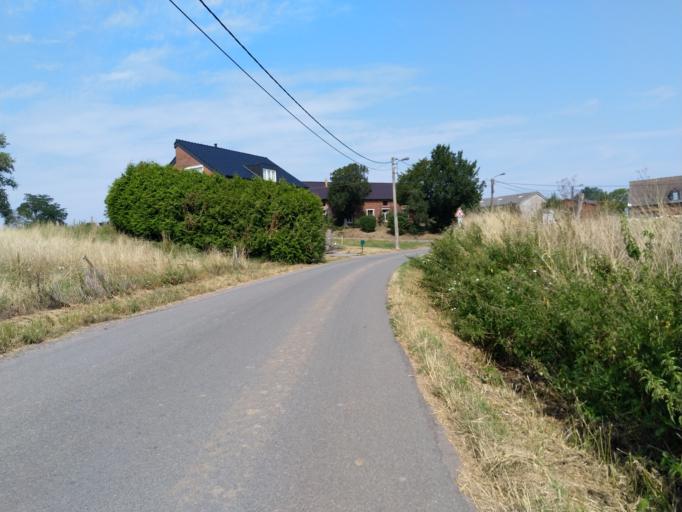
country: BE
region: Wallonia
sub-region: Province du Hainaut
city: Roeulx
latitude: 50.4907
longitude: 4.0559
